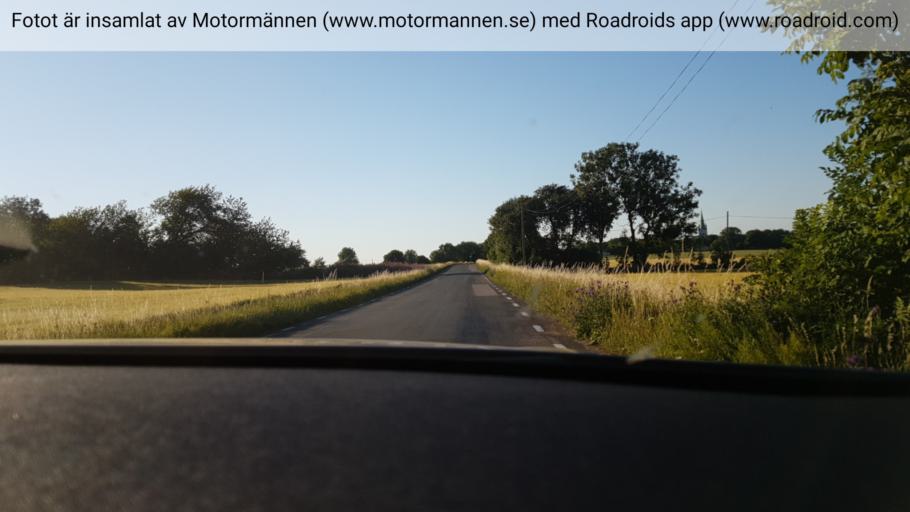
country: SE
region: Vaestra Goetaland
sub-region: Skovde Kommun
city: Skultorp
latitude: 58.2453
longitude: 13.7863
